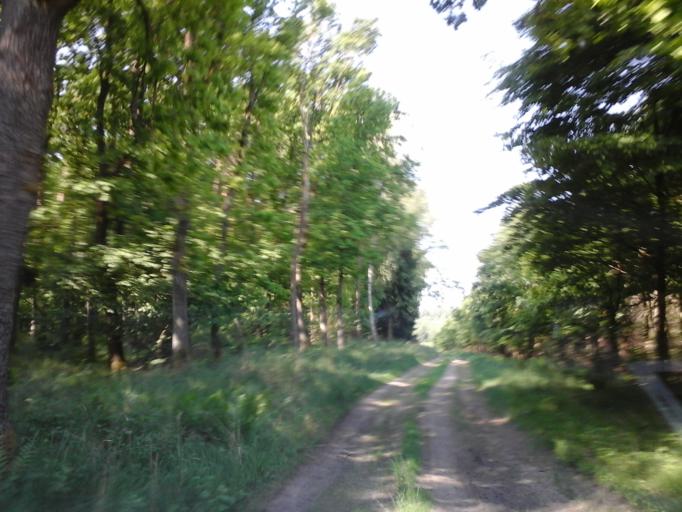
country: PL
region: West Pomeranian Voivodeship
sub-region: Powiat choszczenski
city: Recz
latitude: 53.3183
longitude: 15.5247
